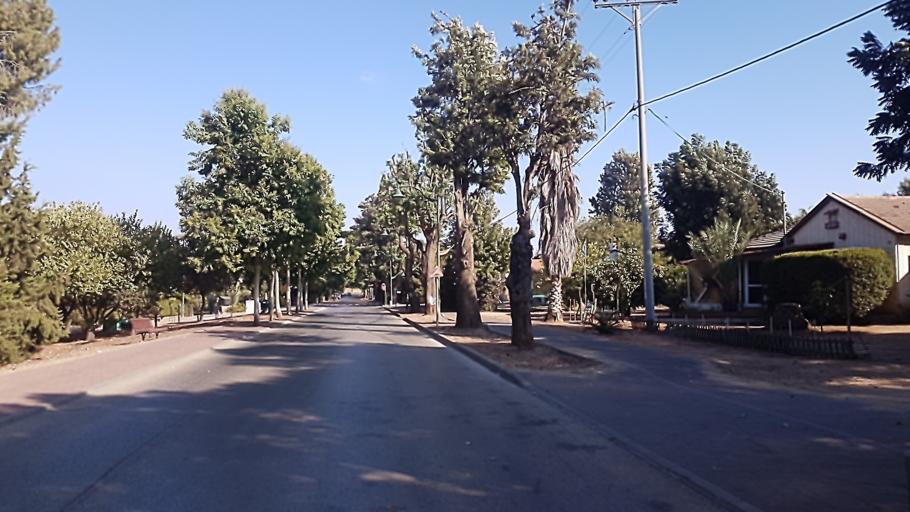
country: IL
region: Central District
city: Kfar Saba
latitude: 32.2100
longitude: 34.9007
